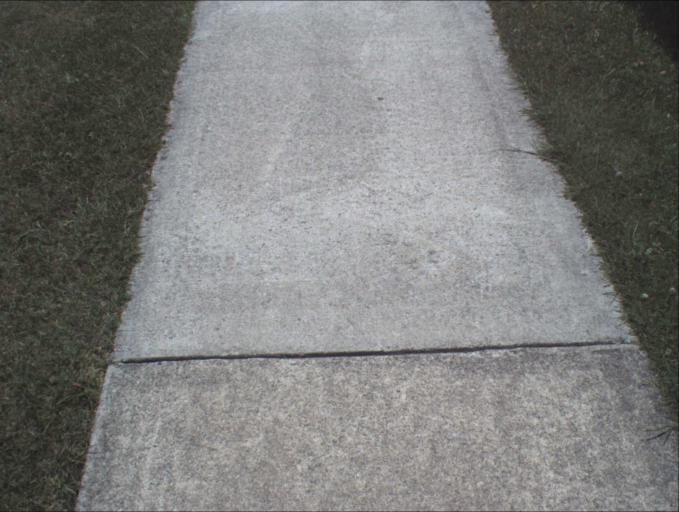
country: AU
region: Queensland
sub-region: Logan
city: Windaroo
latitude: -27.7344
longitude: 153.2115
